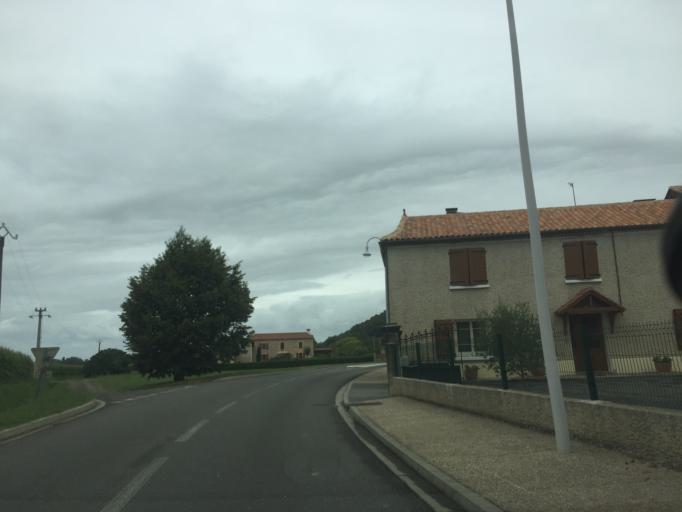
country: FR
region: Midi-Pyrenees
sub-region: Departement des Hautes-Pyrenees
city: Rabastens-de-Bigorre
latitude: 43.3771
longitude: 0.2115
